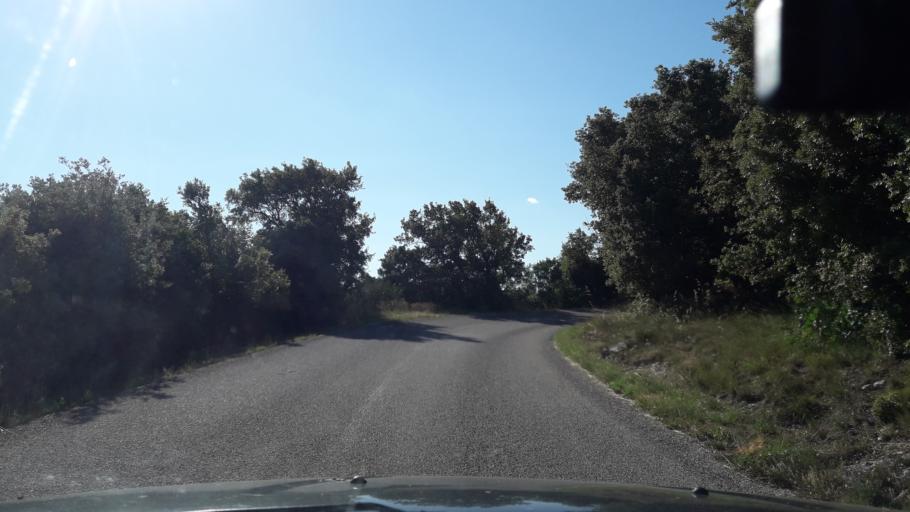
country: FR
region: Languedoc-Roussillon
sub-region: Departement du Gard
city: Saint-Julien-de-Peyrolas
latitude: 44.3780
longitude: 4.5031
